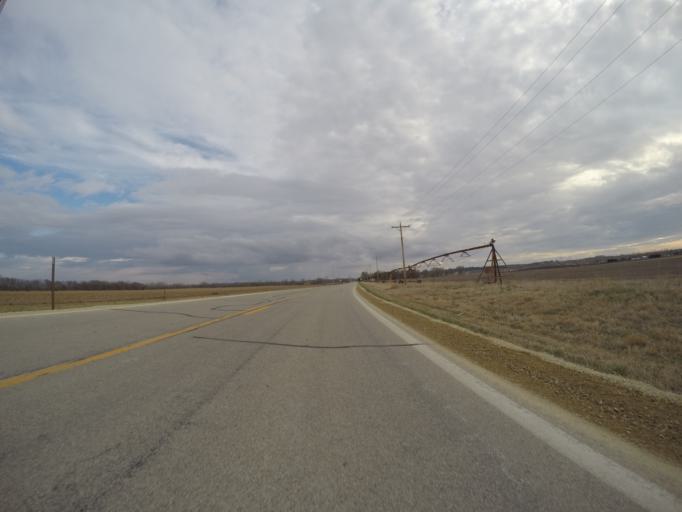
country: US
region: Kansas
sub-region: Riley County
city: Manhattan
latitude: 39.2244
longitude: -96.5578
